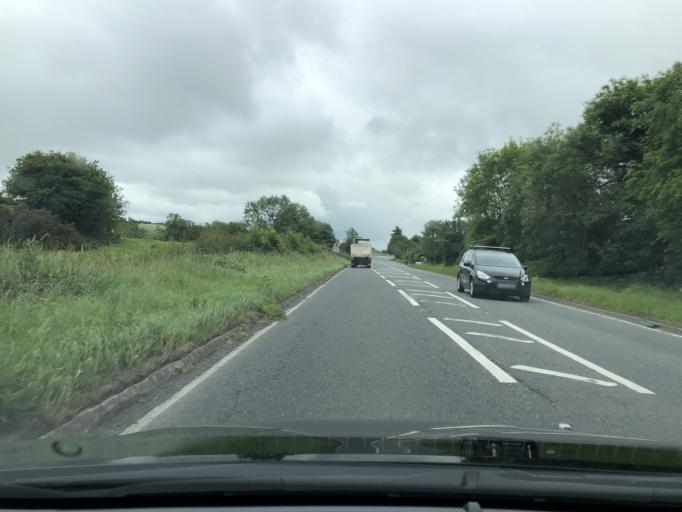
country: GB
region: Northern Ireland
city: Ballynahinch
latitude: 54.3410
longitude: -5.8415
